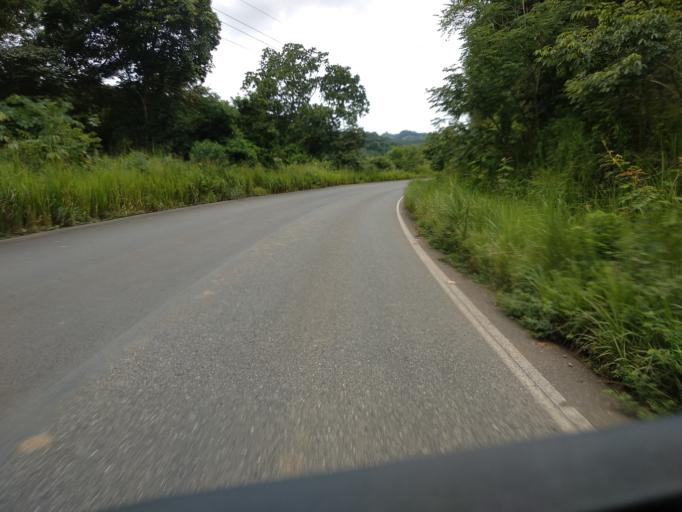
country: CR
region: Puntarenas
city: Buenos Aires
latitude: 9.0901
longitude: -83.2707
